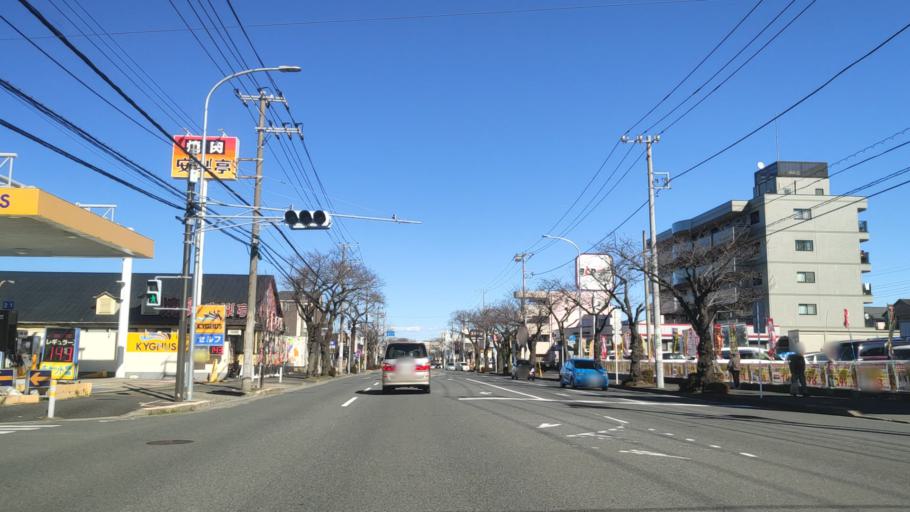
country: JP
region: Tokyo
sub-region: Machida-shi
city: Machida
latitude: 35.5167
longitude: 139.5012
